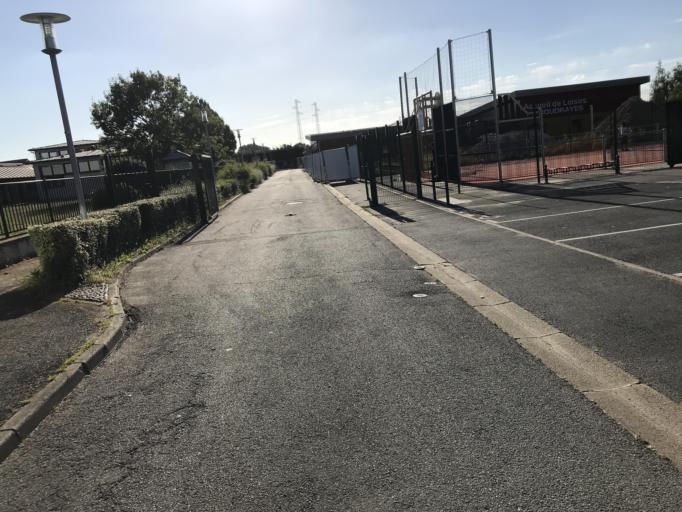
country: FR
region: Ile-de-France
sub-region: Departement de l'Essonne
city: Villejust
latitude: 48.6742
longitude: 2.2161
